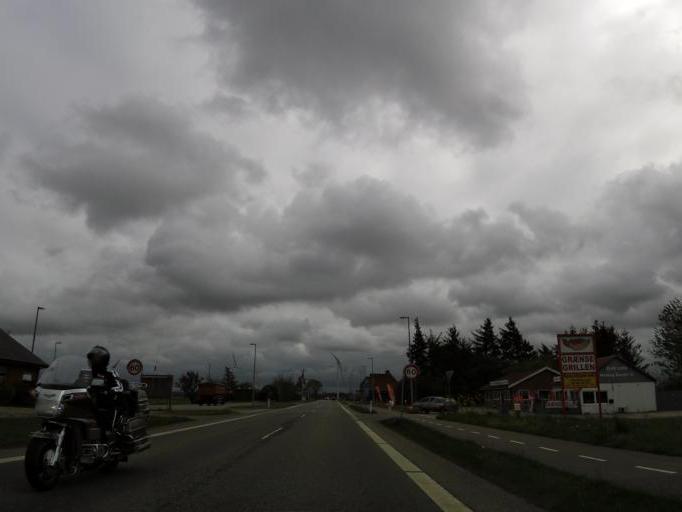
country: DE
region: Schleswig-Holstein
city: Suderlugum
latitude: 54.9056
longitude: 8.9094
